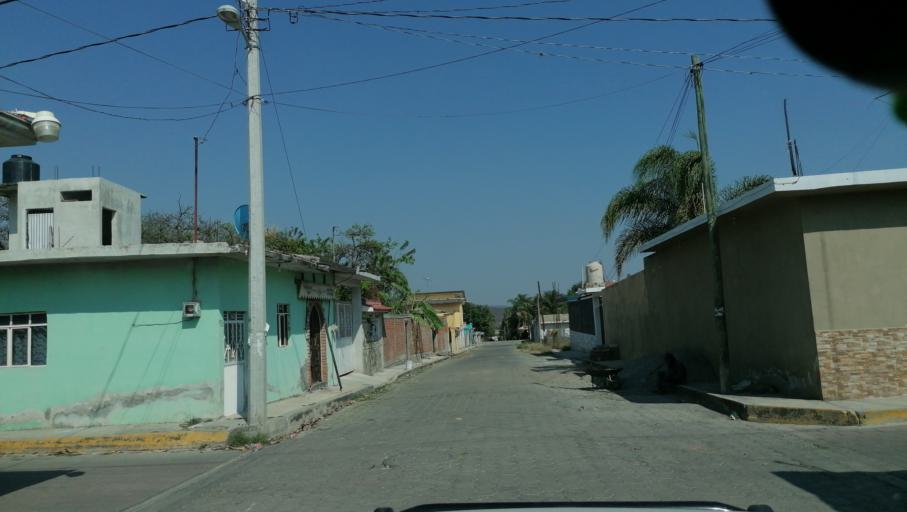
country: MX
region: Puebla
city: Huaquechula
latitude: 18.7722
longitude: -98.5410
